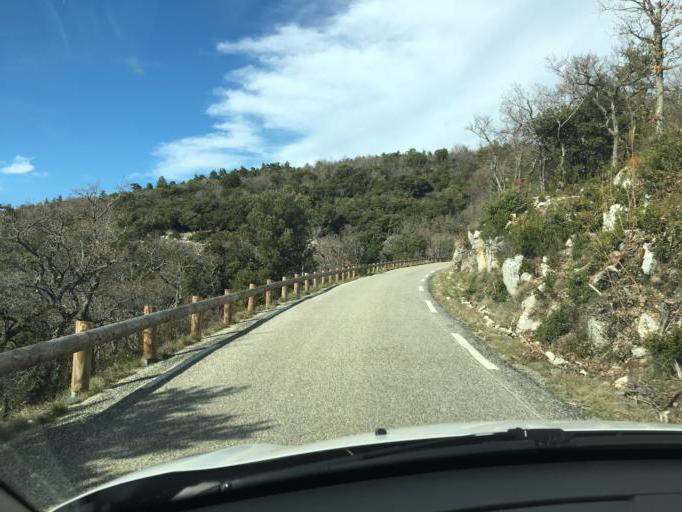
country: FR
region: Provence-Alpes-Cote d'Azur
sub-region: Departement du Vaucluse
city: Saint-Saturnin-les-Apt
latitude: 43.9631
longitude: 5.4615
